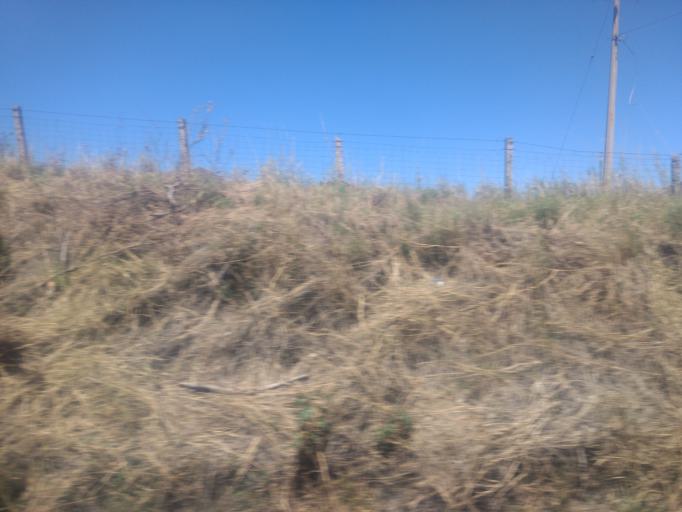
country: MX
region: Jalisco
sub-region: Tlajomulco de Zuniga
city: Santa Cruz de las Flores
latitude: 20.4979
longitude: -103.4888
